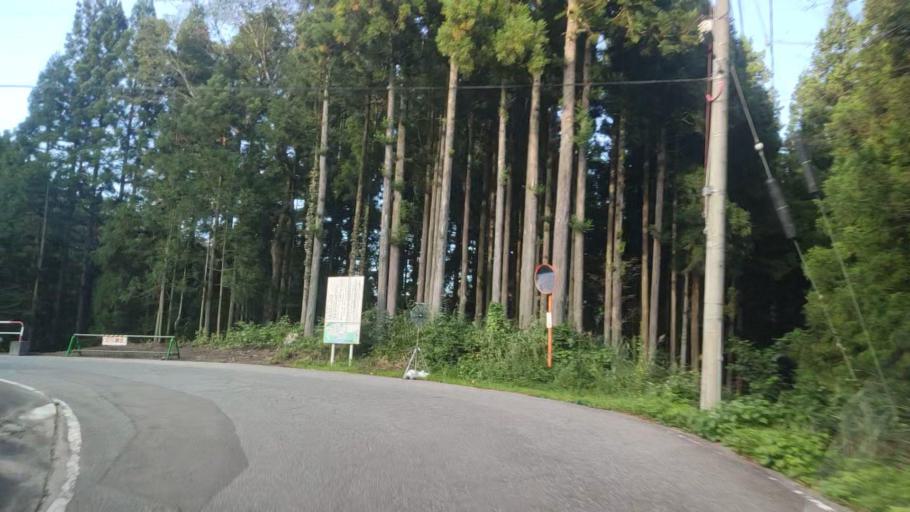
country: JP
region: Toyama
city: Yatsuomachi-higashikumisaka
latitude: 36.5050
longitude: 137.0649
